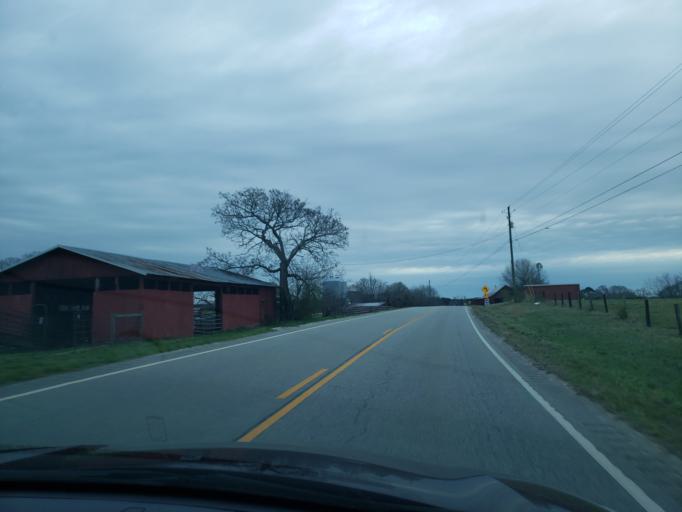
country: US
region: Alabama
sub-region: Chambers County
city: Lafayette
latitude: 32.9914
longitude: -85.3901
